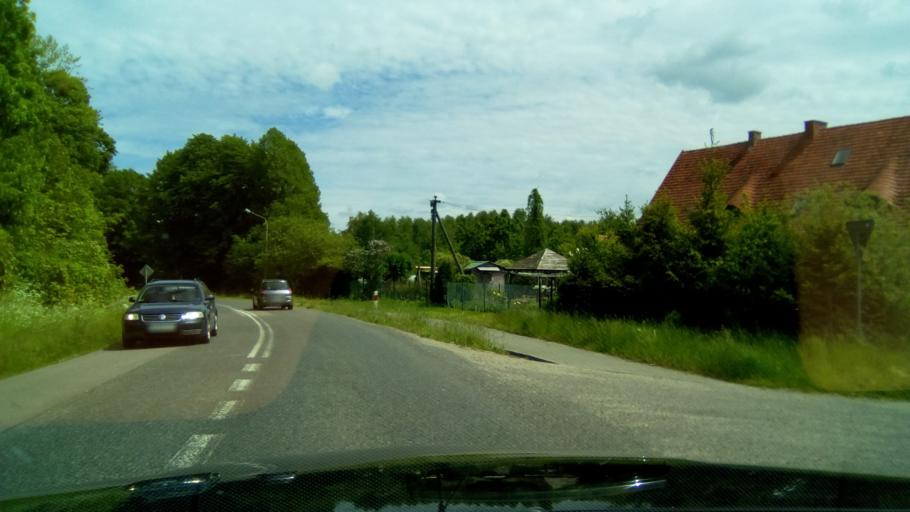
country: PL
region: Pomeranian Voivodeship
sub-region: Powiat leborski
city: Cewice
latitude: 54.4386
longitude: 17.7469
